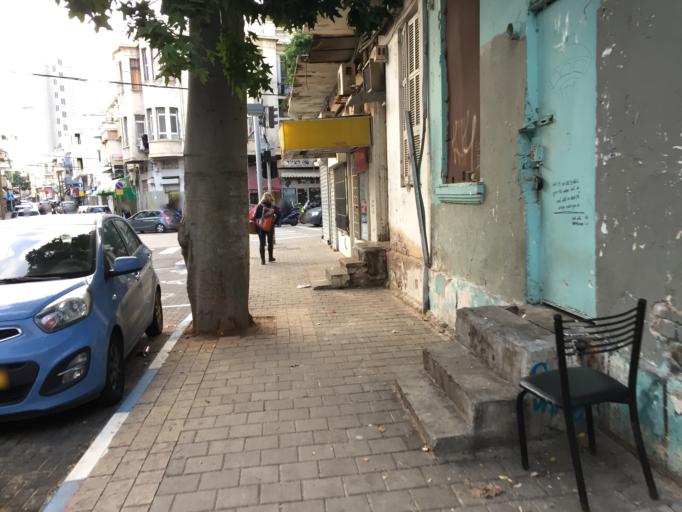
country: IL
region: Tel Aviv
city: Yafo
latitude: 32.0586
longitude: 34.7739
